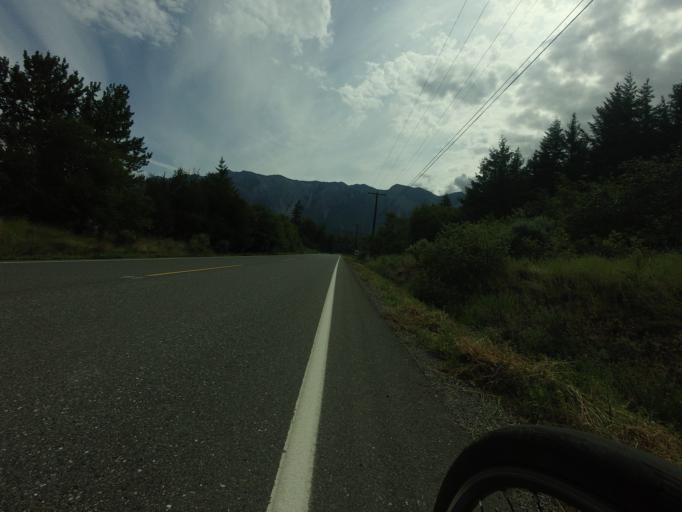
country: CA
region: British Columbia
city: Lillooet
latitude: 50.6711
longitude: -121.9461
